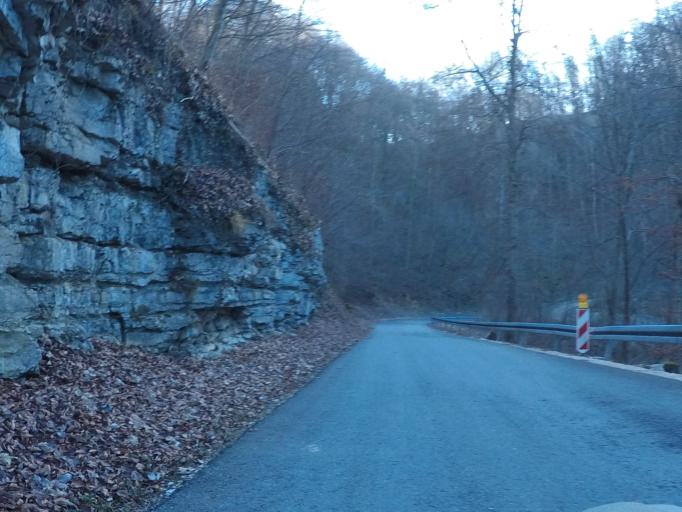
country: DE
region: Baden-Wuerttemberg
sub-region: Tuebingen Region
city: Sankt Johann
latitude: 48.4434
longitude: 9.2959
